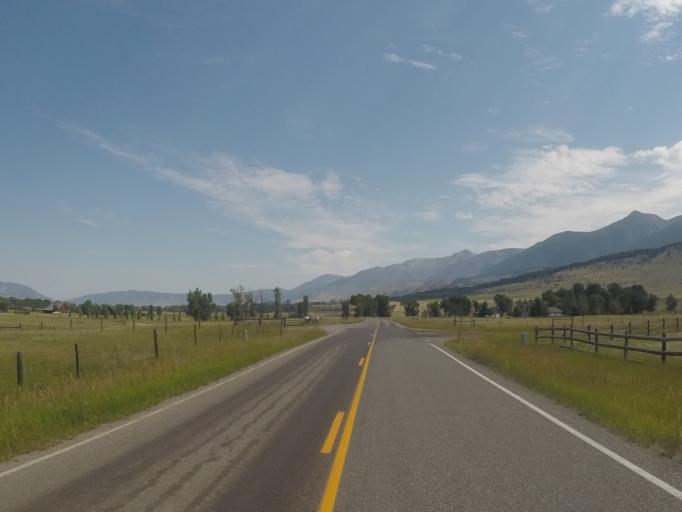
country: US
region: Montana
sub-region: Park County
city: Livingston
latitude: 45.4312
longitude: -110.6153
